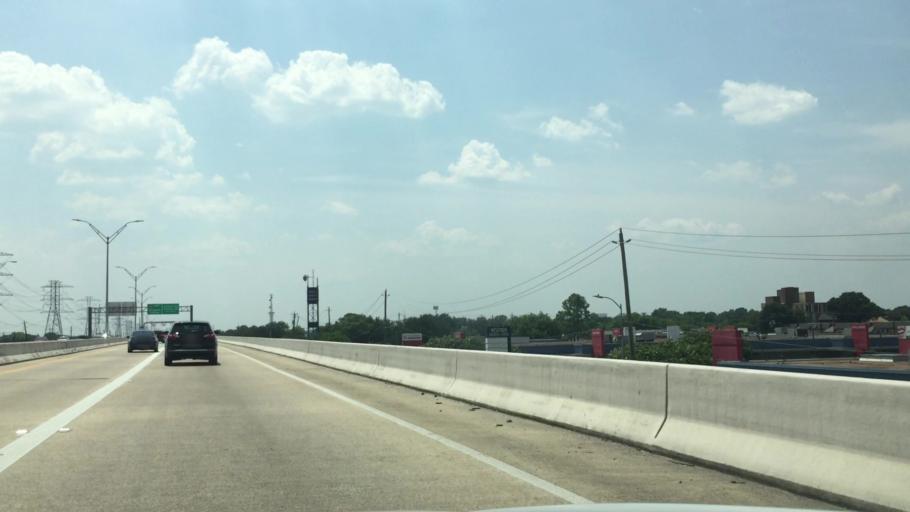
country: US
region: Texas
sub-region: Harris County
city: Piney Point Village
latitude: 29.7232
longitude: -95.4980
